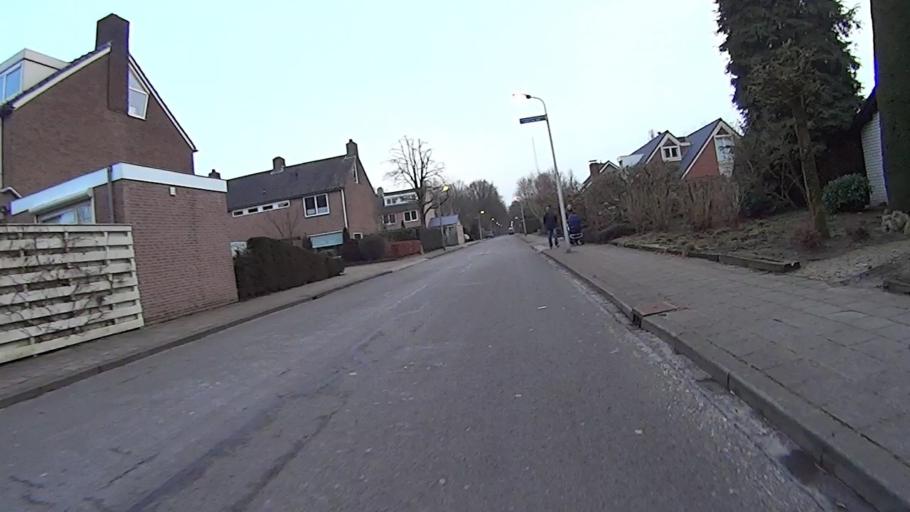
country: NL
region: Utrecht
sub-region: Gemeente Amersfoort
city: Randenbroek
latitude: 52.1408
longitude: 5.3993
